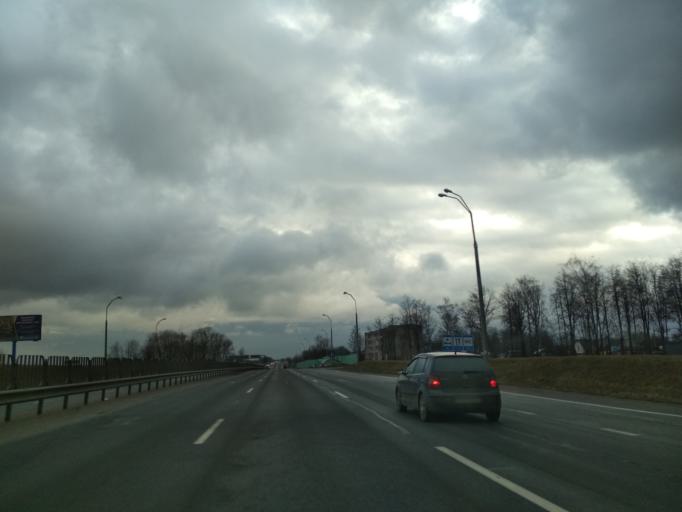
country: BY
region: Minsk
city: Pryvol'ny
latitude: 53.8019
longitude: 27.7995
